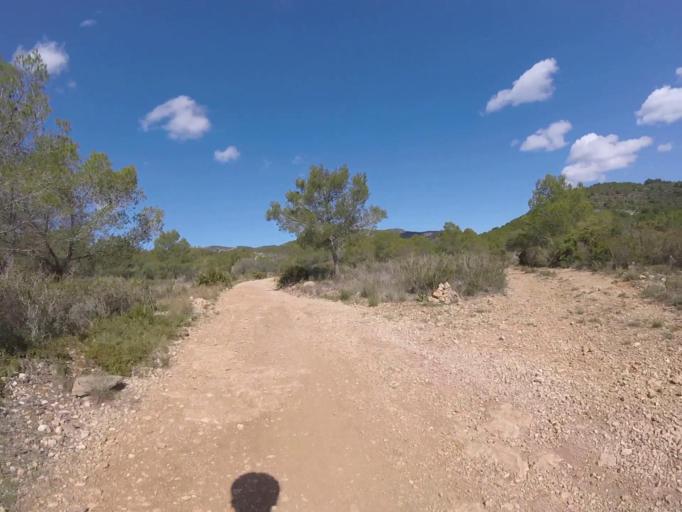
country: ES
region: Valencia
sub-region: Provincia de Castello
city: Alcoceber
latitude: 40.2896
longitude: 0.3177
